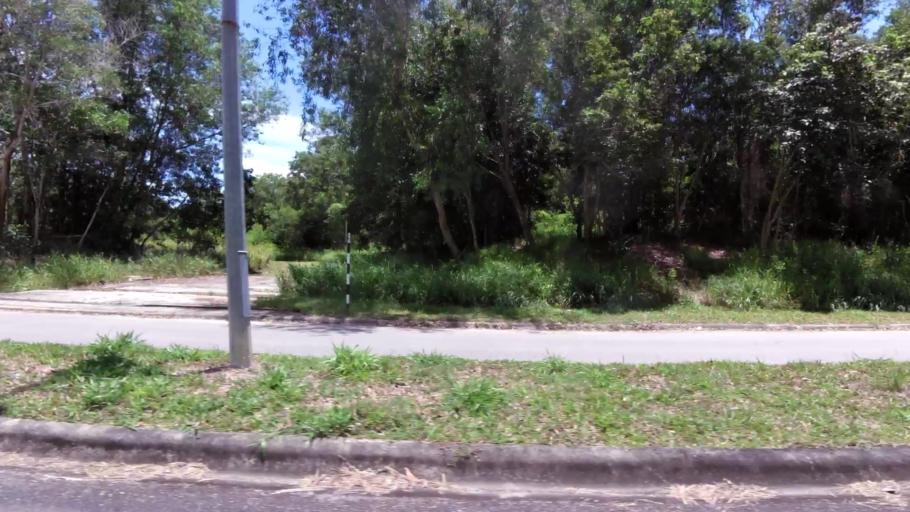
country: BN
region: Brunei and Muara
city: Bandar Seri Begawan
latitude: 4.9519
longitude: 114.8963
